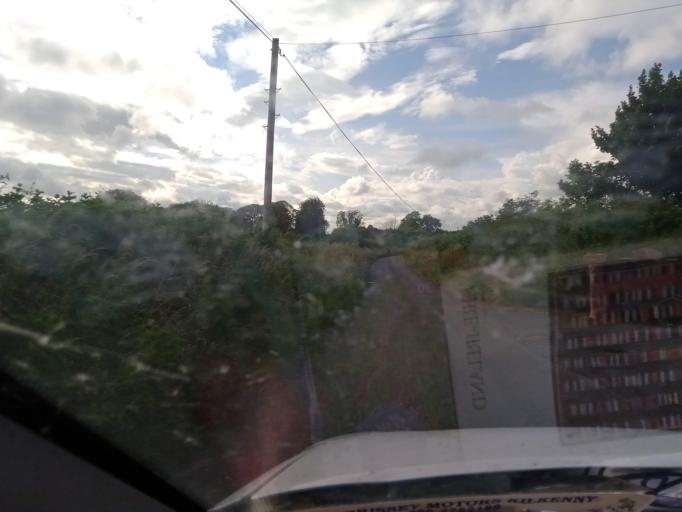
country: IE
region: Leinster
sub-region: Laois
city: Rathdowney
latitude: 52.7877
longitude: -7.5534
